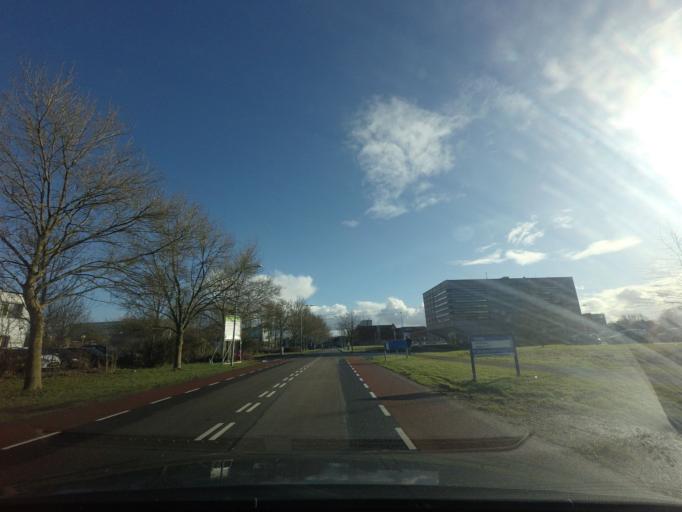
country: NL
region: Groningen
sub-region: Gemeente Groningen
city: Korrewegwijk
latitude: 53.2433
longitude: 6.5324
